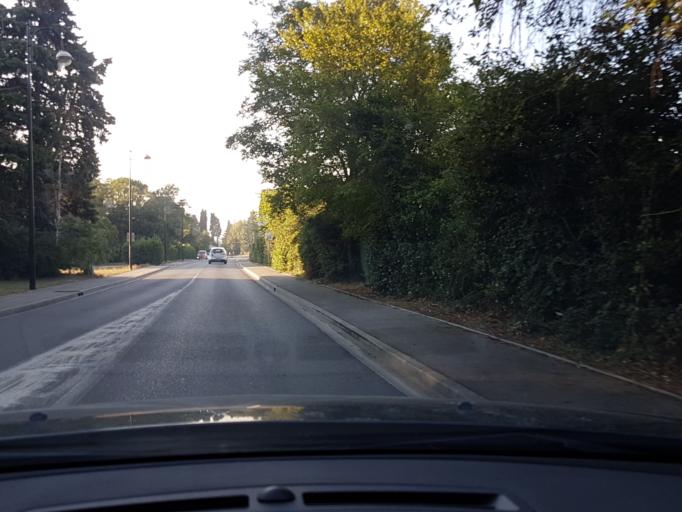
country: FR
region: Provence-Alpes-Cote d'Azur
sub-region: Departement des Bouches-du-Rhone
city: Molleges
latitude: 43.8034
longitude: 4.9502
